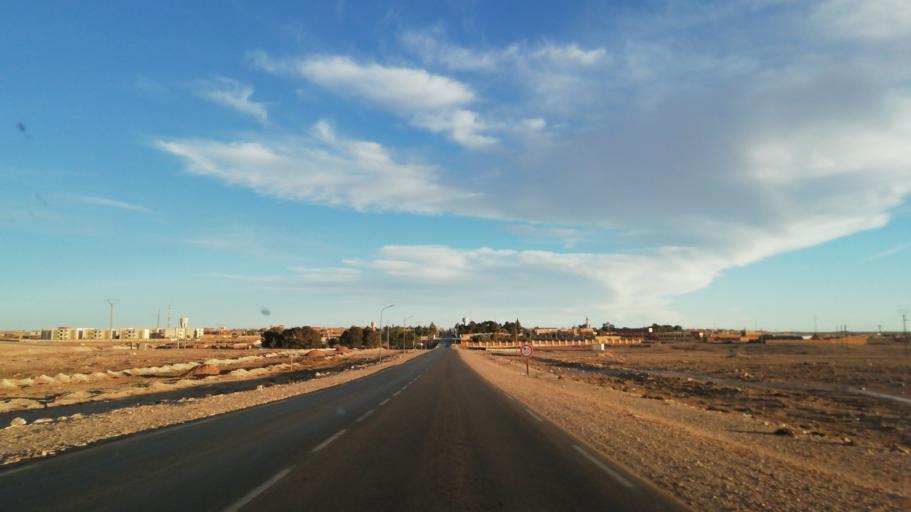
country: DZ
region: Wilaya de Naama
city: Naama
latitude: 33.7224
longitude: -0.7371
